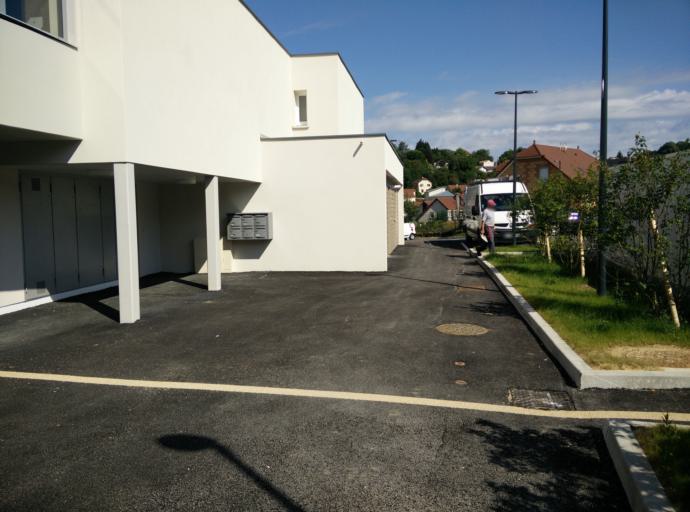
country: FR
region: Franche-Comte
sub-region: Departement du Doubs
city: Besancon
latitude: 47.2643
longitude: 6.0266
